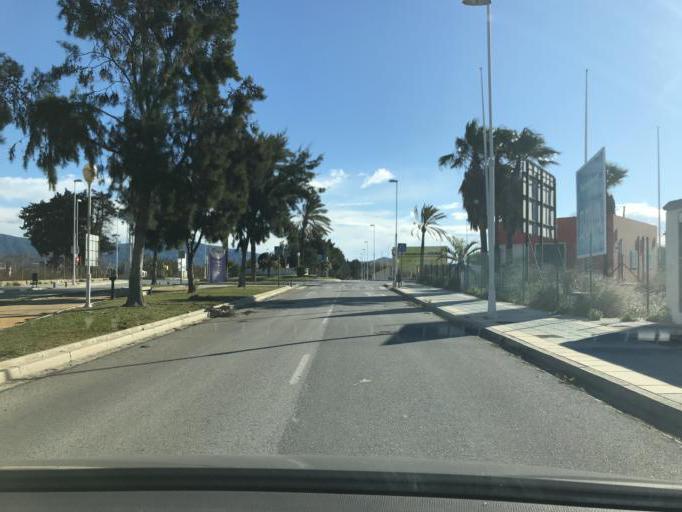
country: ES
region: Andalusia
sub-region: Provincia de Granada
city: Salobrena
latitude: 36.7237
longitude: -3.5603
